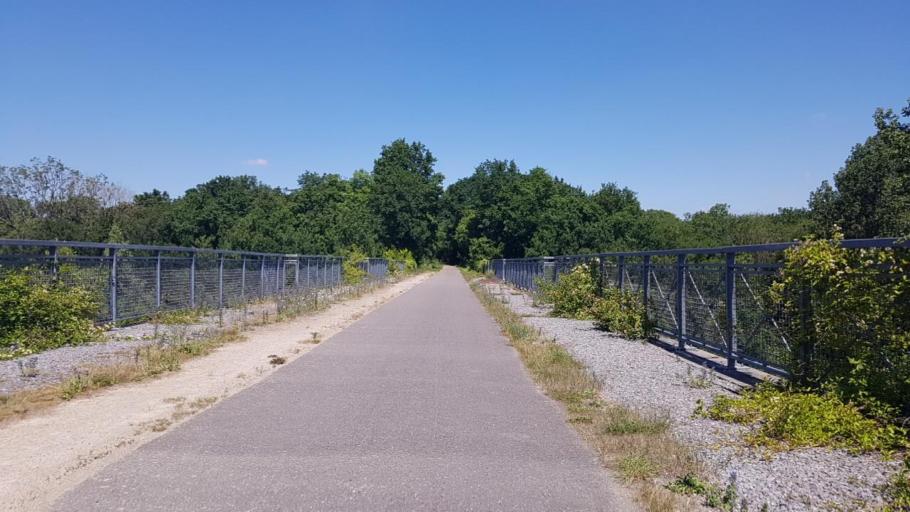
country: BE
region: Wallonia
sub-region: Province du Hainaut
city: Beaumont
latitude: 50.2229
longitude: 4.2433
